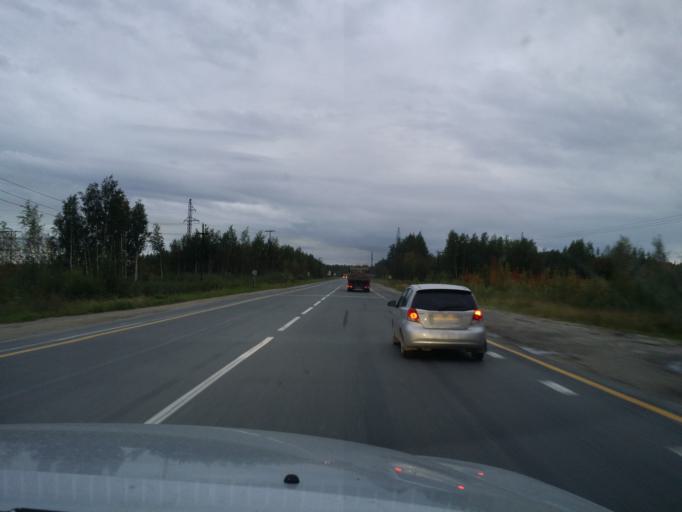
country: RU
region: Khanty-Mansiyskiy Avtonomnyy Okrug
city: Izluchinsk
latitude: 61.0095
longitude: 76.7702
